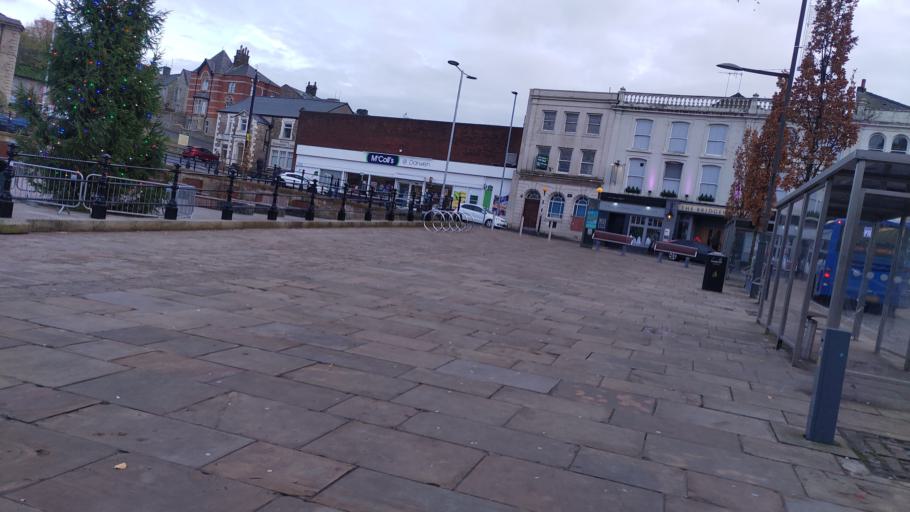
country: GB
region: England
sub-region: Blackburn with Darwen
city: Darwen
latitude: 53.6957
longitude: -2.4668
